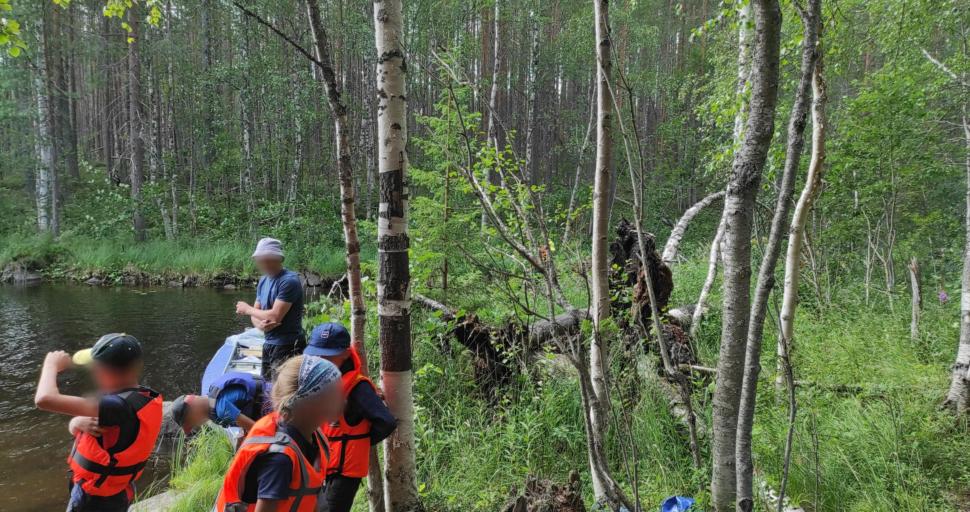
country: RU
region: Murmansk
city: Zelenoborskiy
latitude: 66.7154
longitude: 32.4532
